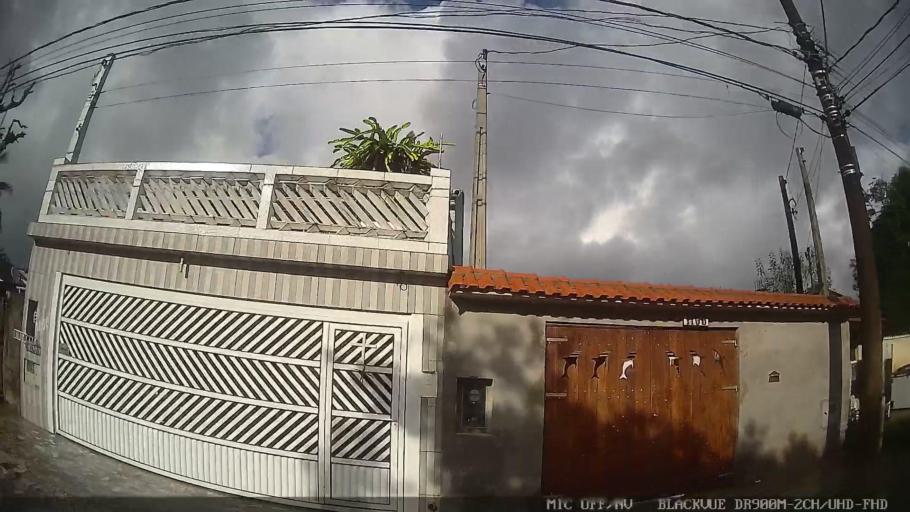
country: BR
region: Sao Paulo
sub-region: Itanhaem
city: Itanhaem
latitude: -24.2280
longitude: -46.8925
